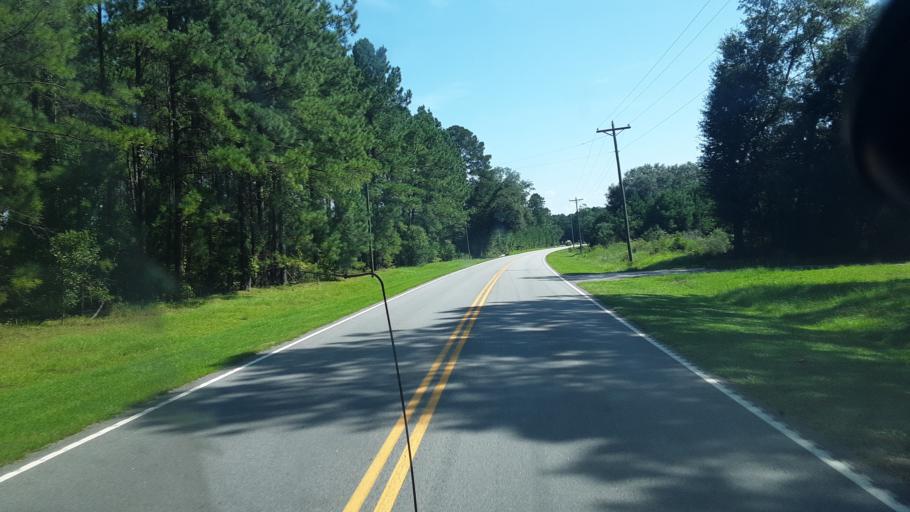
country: US
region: South Carolina
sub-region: Hampton County
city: Varnville
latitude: 32.8637
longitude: -81.0668
